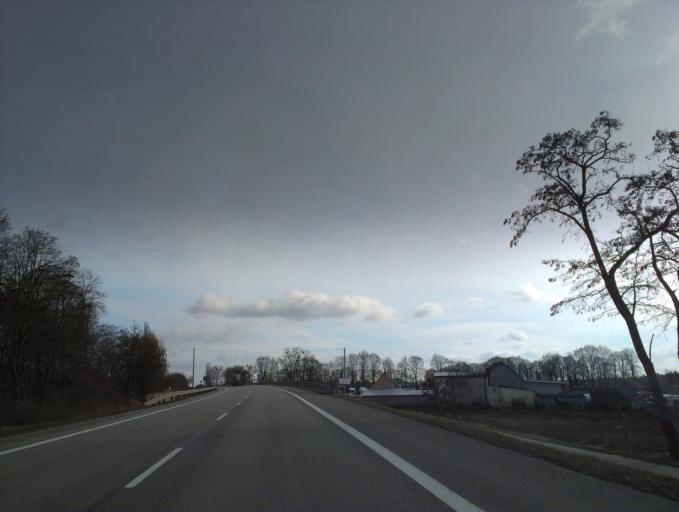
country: PL
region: Kujawsko-Pomorskie
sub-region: Powiat lipnowski
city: Lipno
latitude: 52.8561
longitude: 19.1611
